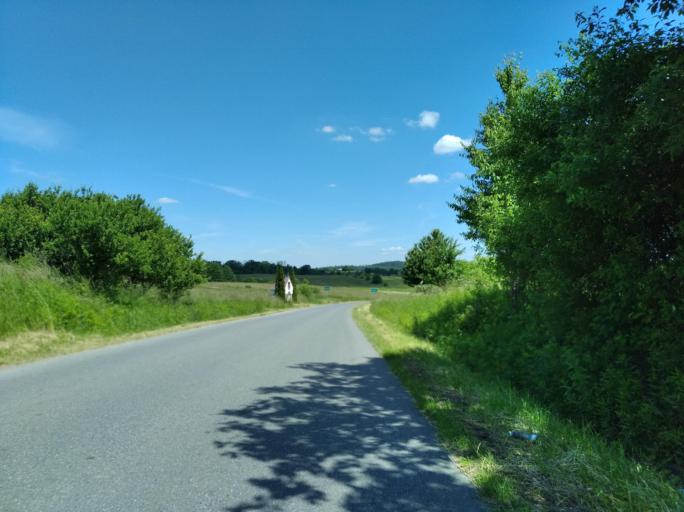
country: PL
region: Subcarpathian Voivodeship
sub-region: Powiat jasielski
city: Osiek Jasielski
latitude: 49.6611
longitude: 21.5345
